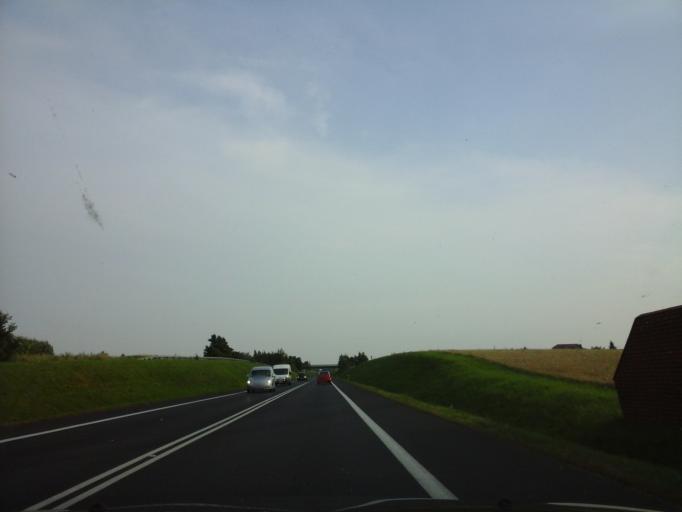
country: PL
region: Greater Poland Voivodeship
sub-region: Powiat koscianski
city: Smigiel
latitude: 52.0135
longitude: 16.5421
